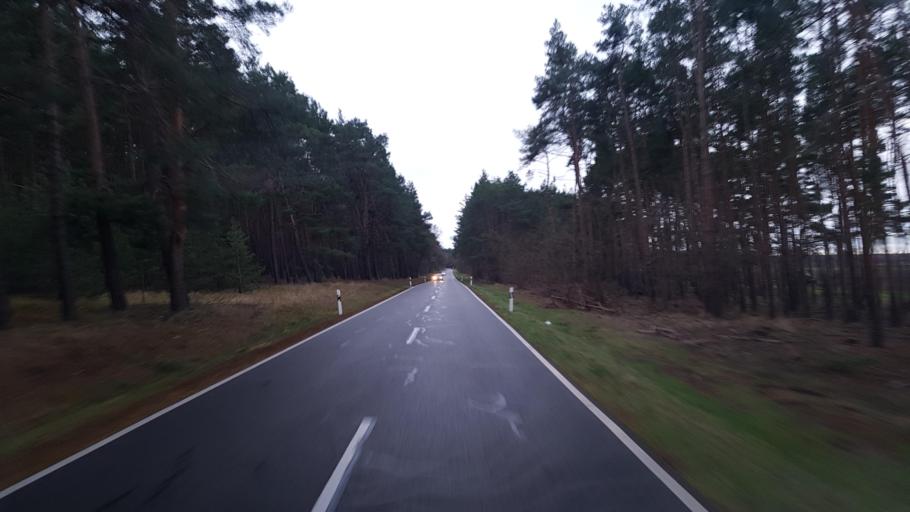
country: DE
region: Brandenburg
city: Schlepzig
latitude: 52.0121
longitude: 13.9754
